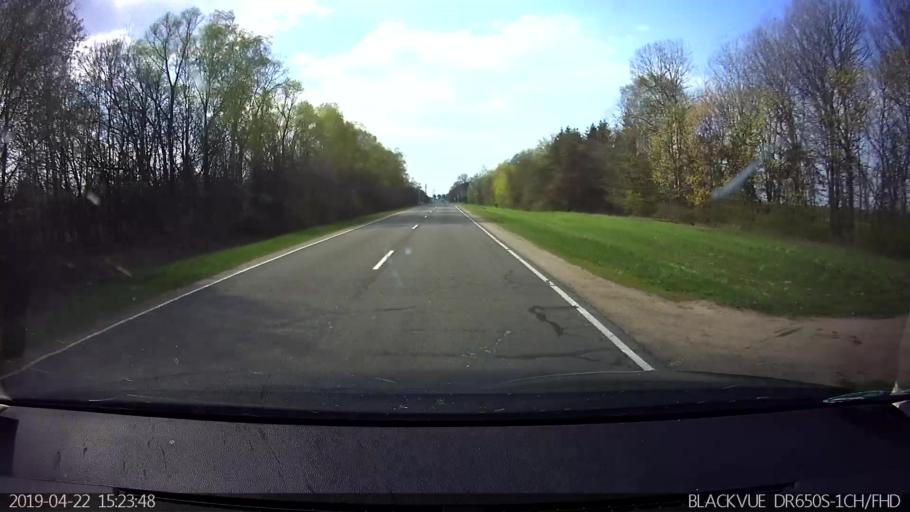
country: BY
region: Brest
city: Vysokaye
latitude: 52.3574
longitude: 23.4193
